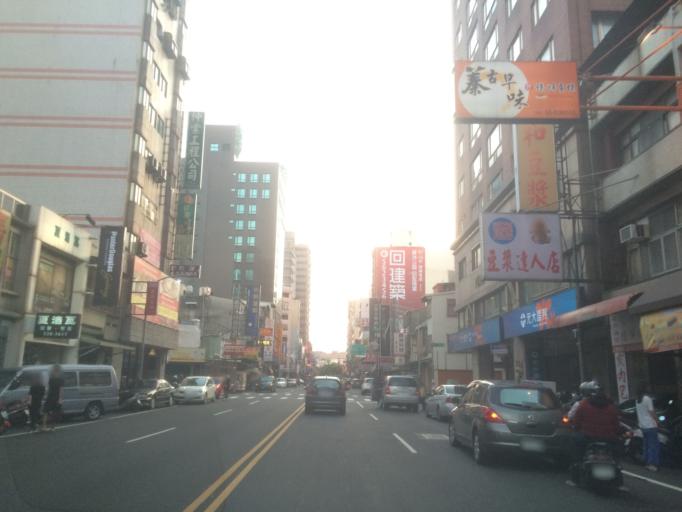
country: TW
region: Taiwan
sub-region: Hsinchu
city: Hsinchu
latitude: 24.7990
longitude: 120.9642
